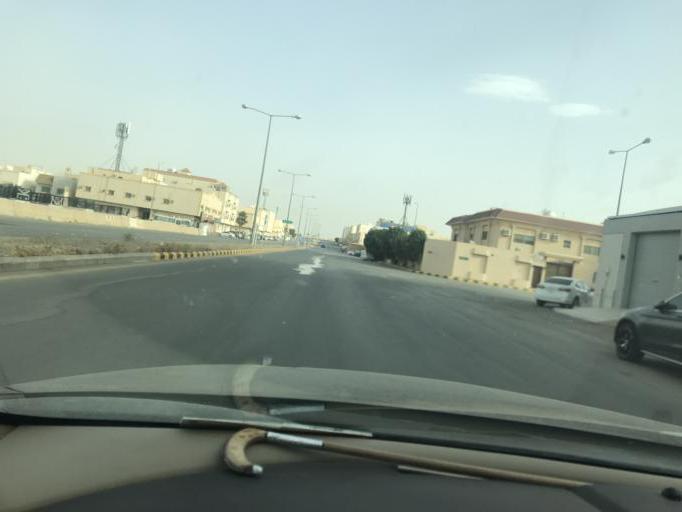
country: SA
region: Ar Riyad
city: Riyadh
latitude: 24.7856
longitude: 46.7136
